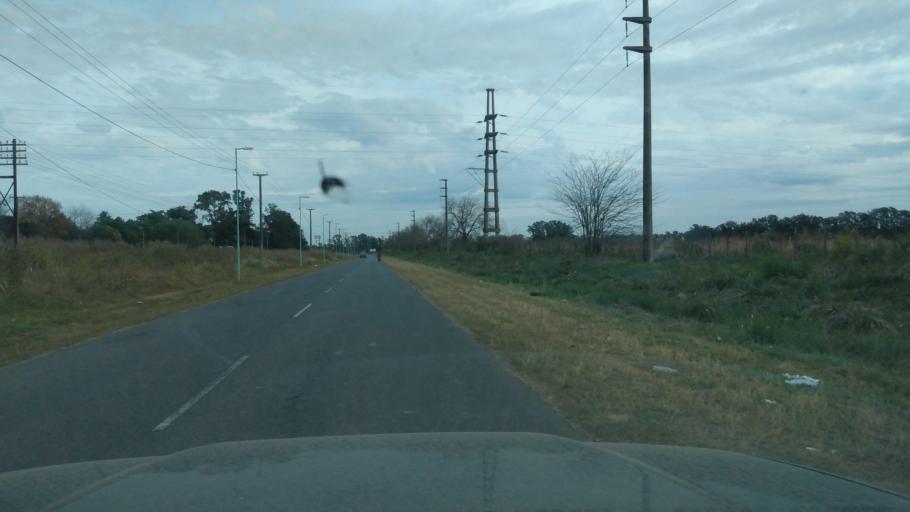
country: AR
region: Buenos Aires
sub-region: Partido de Lujan
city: Lujan
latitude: -34.5887
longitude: -59.1386
